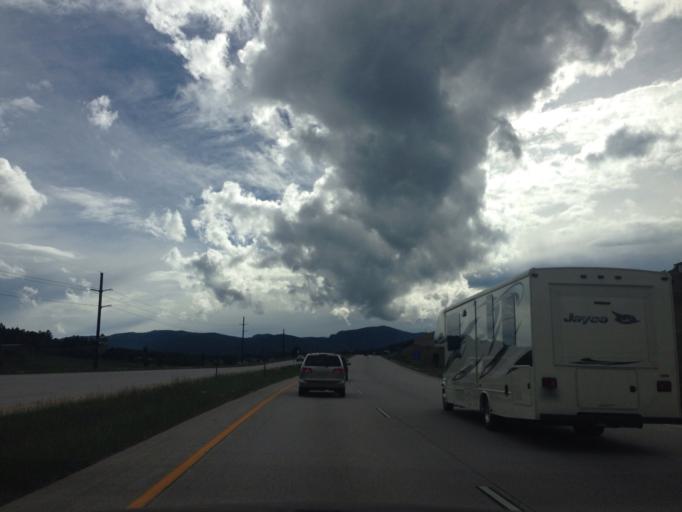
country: US
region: Colorado
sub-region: Jefferson County
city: Indian Hills
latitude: 39.5435
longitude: -105.2849
